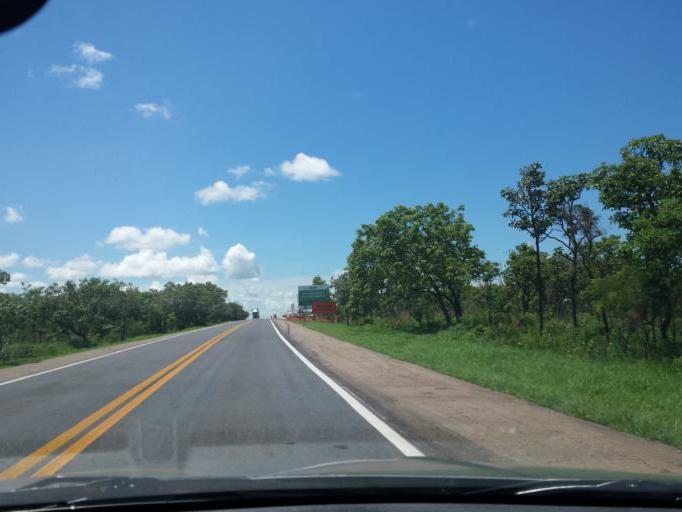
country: BR
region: Goias
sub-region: Luziania
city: Luziania
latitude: -16.4512
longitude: -47.8080
